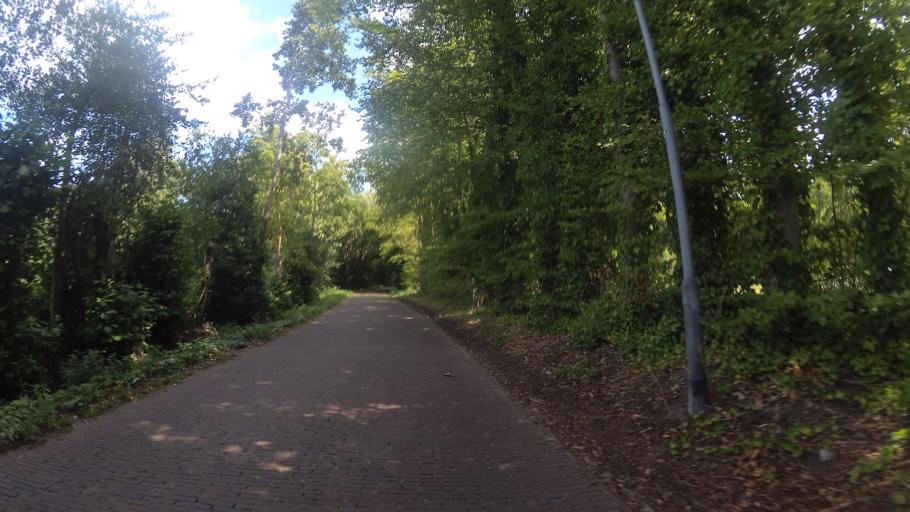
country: NL
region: Zeeland
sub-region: Schouwen-Duiveland
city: Haamstede
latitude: 51.7137
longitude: 3.7524
